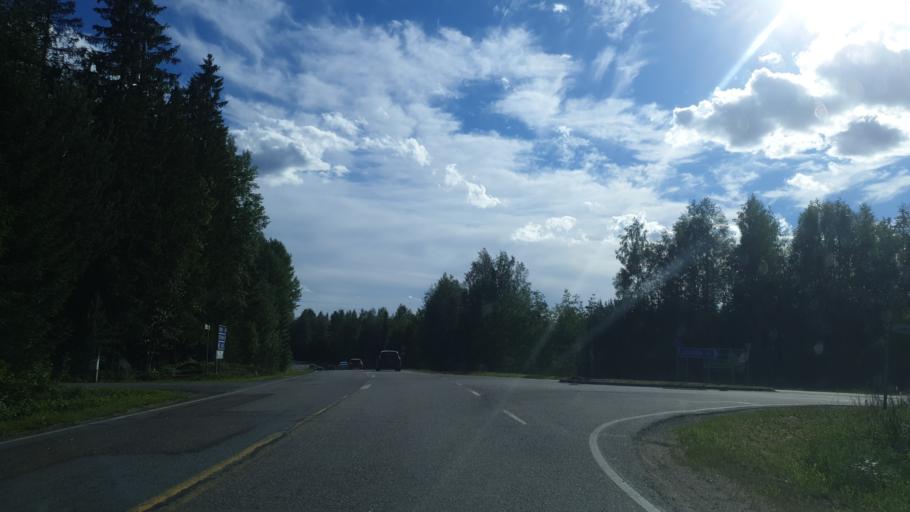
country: FI
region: Southern Savonia
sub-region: Mikkeli
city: Pertunmaa
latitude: 61.5181
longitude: 26.4900
